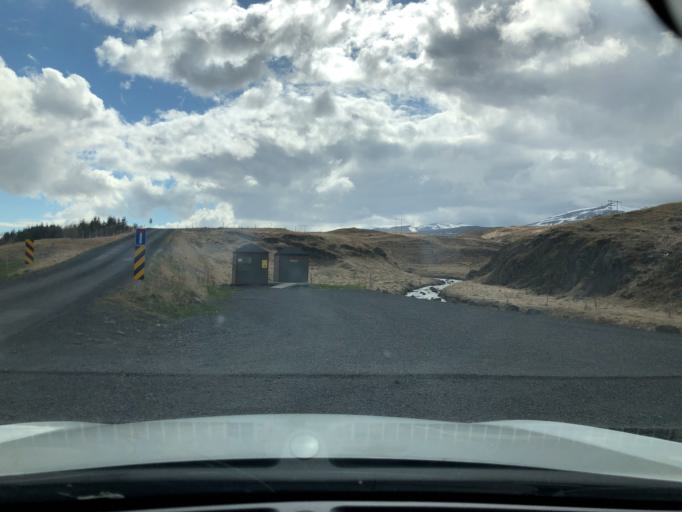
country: IS
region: Northwest
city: Saudarkrokur
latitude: 65.5388
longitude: -19.4713
